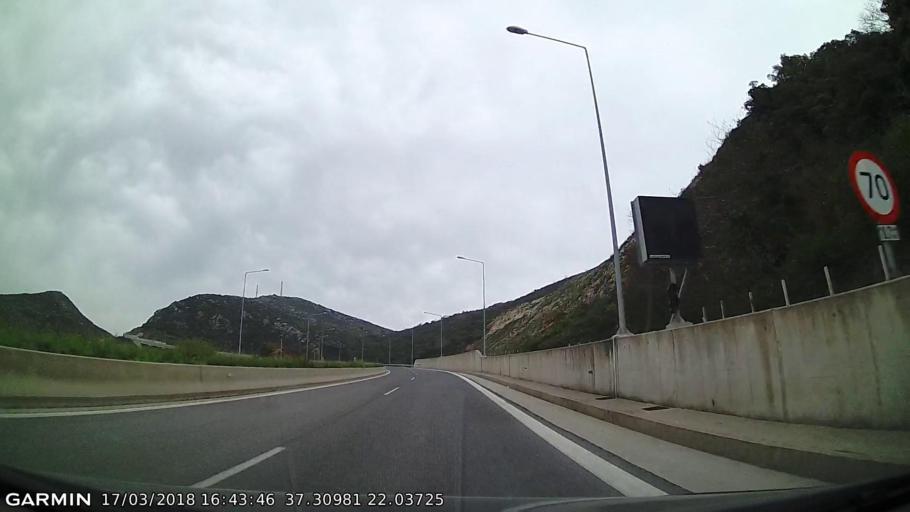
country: GR
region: Peloponnese
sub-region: Nomos Messinias
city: Meligalas
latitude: 37.3105
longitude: 22.0384
